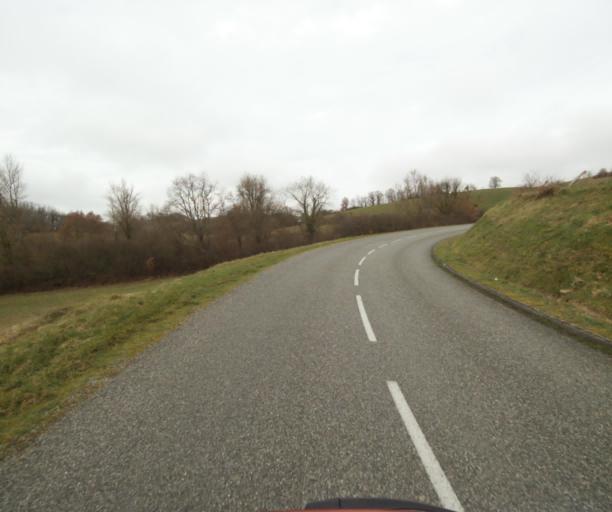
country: FR
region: Midi-Pyrenees
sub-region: Departement de l'Ariege
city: Pamiers
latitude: 43.1489
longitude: 1.5153
